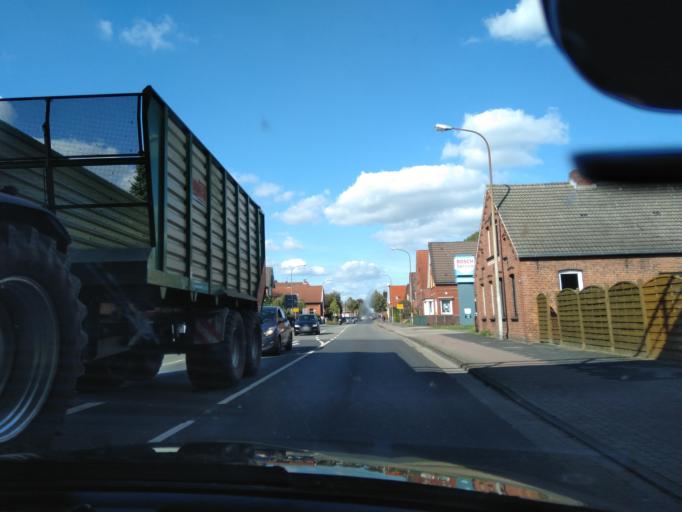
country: DE
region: Lower Saxony
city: Leer
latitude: 53.2397
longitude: 7.4561
